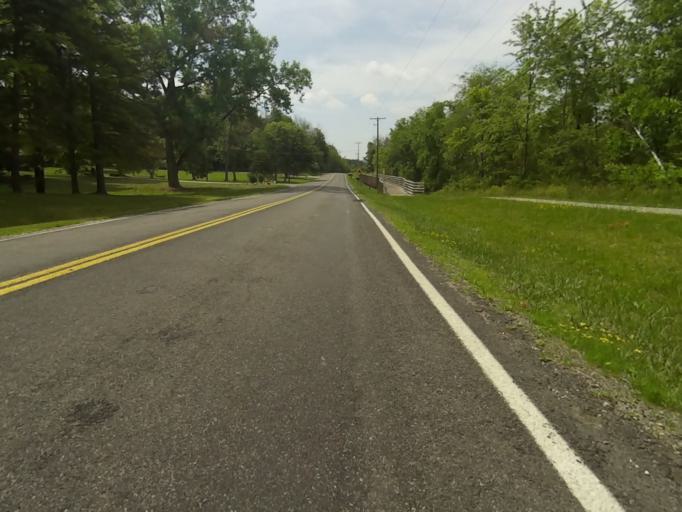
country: US
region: Ohio
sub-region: Summit County
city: Boston Heights
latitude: 41.2816
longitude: -81.5384
